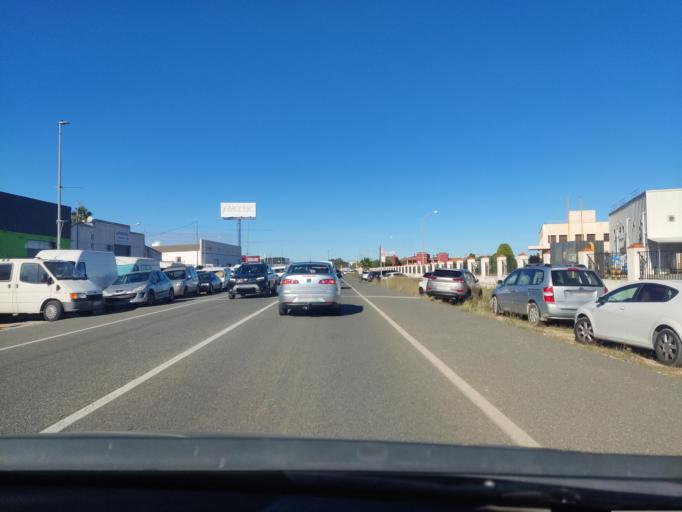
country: ES
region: Valencia
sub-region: Provincia de Alicante
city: Vergel
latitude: 38.8563
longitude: -0.0012
